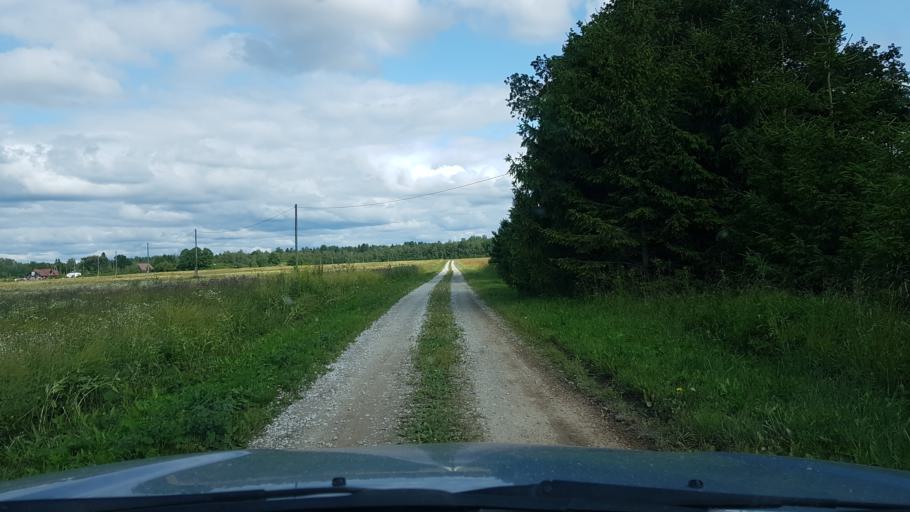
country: EE
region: Ida-Virumaa
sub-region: Narva-Joesuu linn
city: Narva-Joesuu
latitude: 59.3701
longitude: 27.9466
